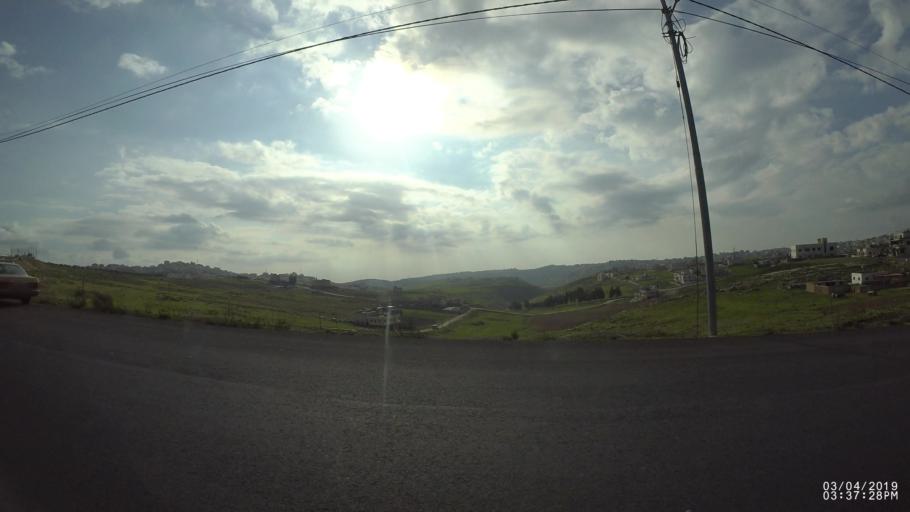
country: JO
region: Amman
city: Wadi as Sir
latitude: 31.9281
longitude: 35.8490
